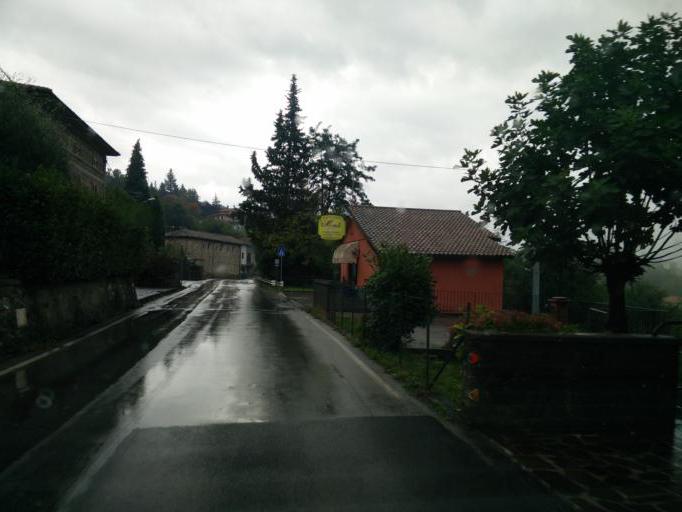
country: IT
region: Tuscany
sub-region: Provincia di Lucca
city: San Romano in Garfagnana
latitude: 44.1649
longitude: 10.3532
